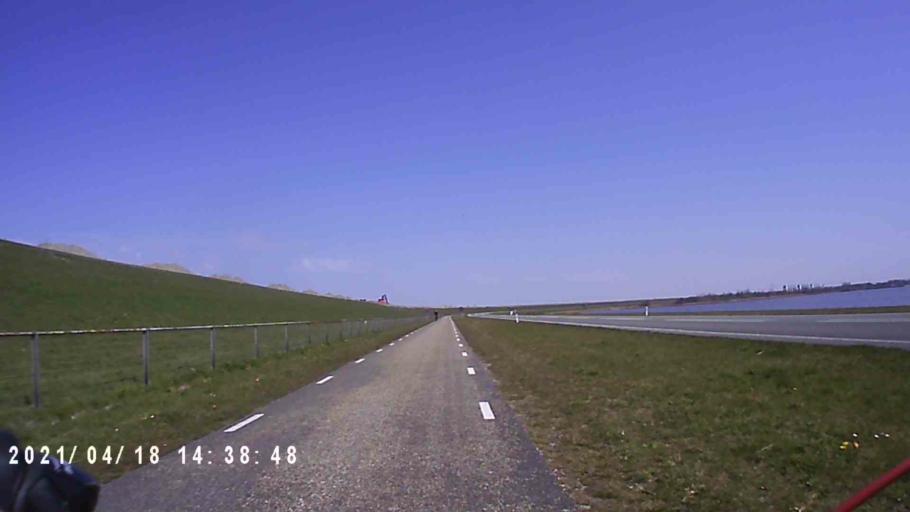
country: NL
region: Friesland
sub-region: Gemeente Dongeradeel
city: Anjum
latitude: 53.4135
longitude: 6.1708
